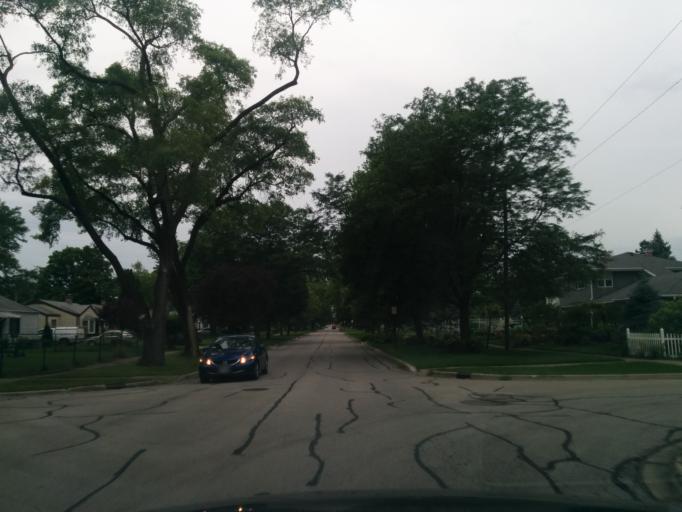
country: US
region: Illinois
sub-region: DuPage County
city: Villa Park
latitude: 41.8751
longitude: -87.9851
